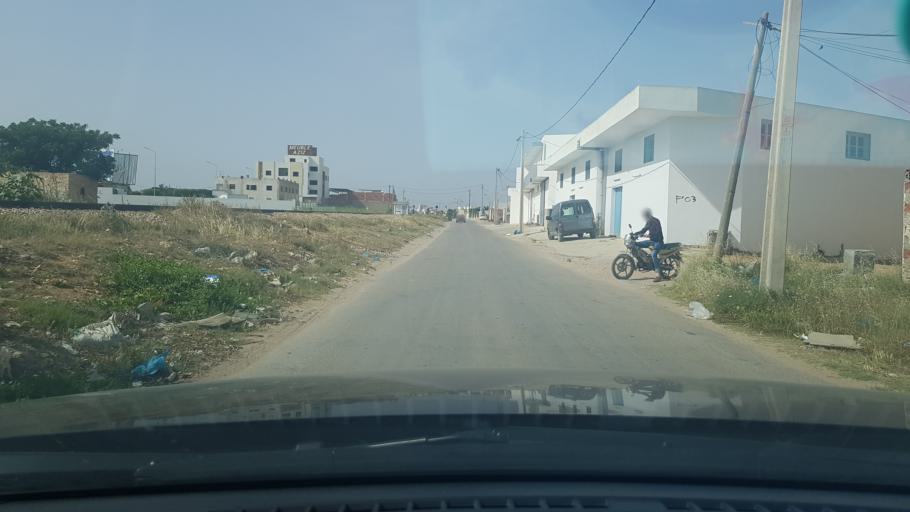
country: TN
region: Safaqis
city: Al Qarmadah
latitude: 34.8243
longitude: 10.7641
